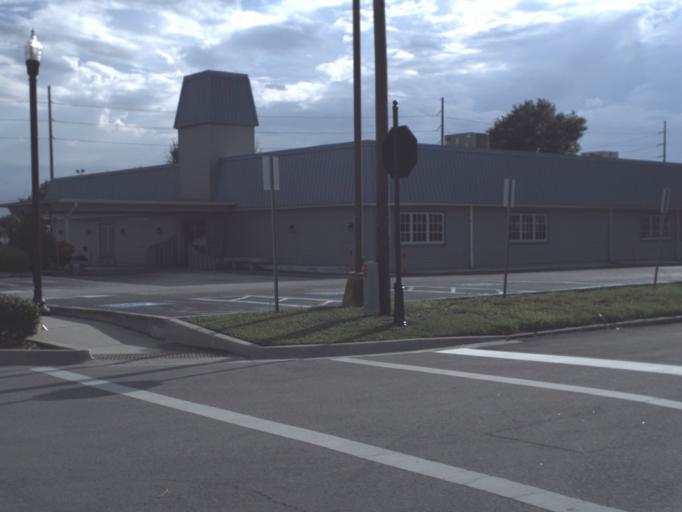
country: US
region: Florida
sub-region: Polk County
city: Winter Haven
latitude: 28.0178
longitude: -81.7307
